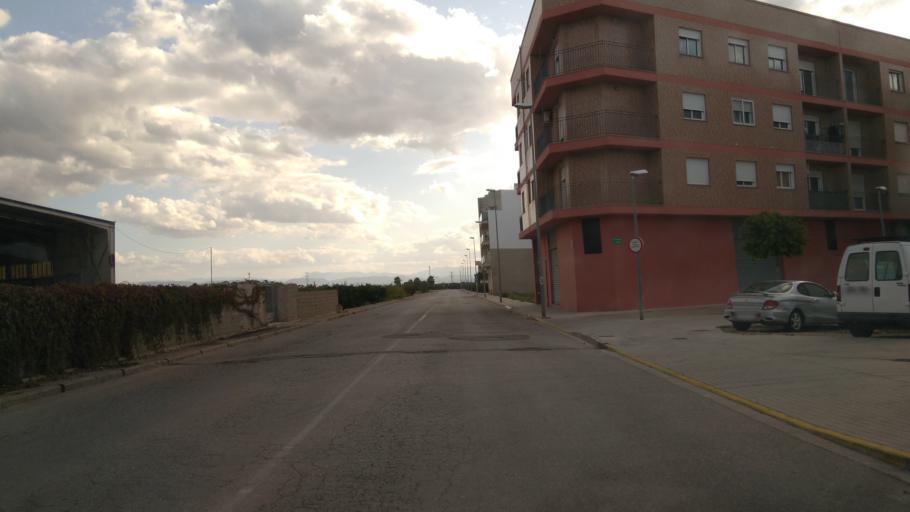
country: ES
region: Valencia
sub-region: Provincia de Valencia
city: L'Alcudia
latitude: 39.1947
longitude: -0.4991
